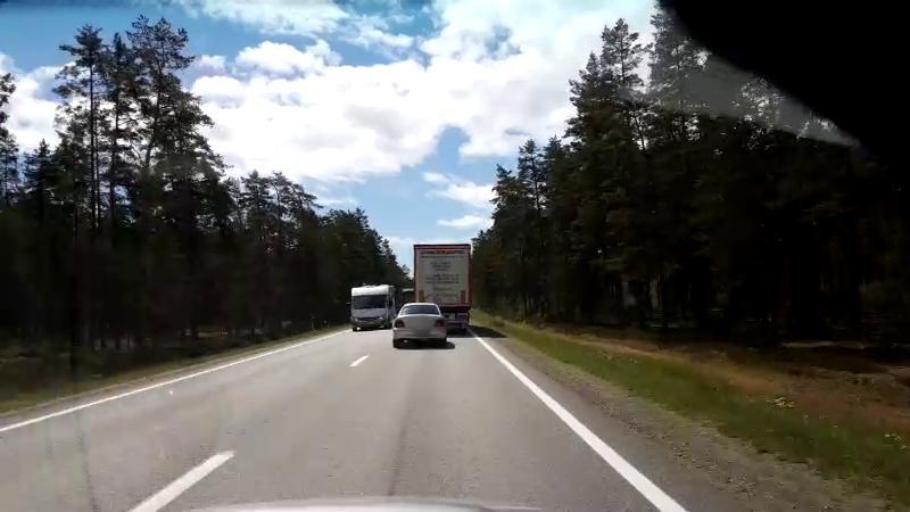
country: LV
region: Salacgrivas
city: Salacgriva
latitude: 57.5561
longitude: 24.4334
